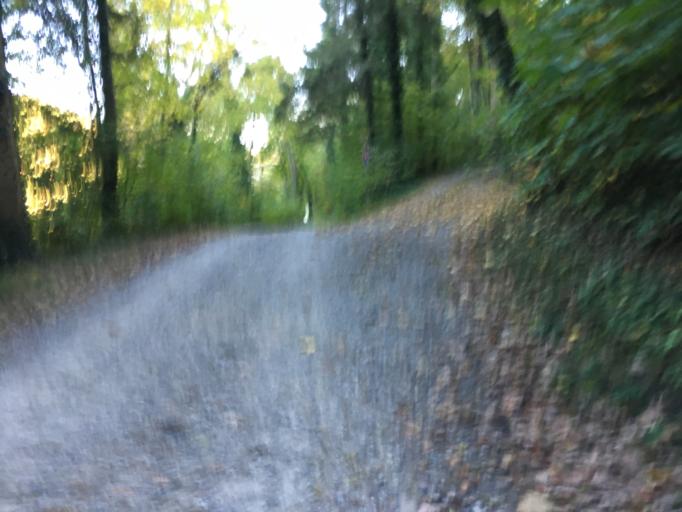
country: CH
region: Zurich
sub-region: Bezirk Buelach
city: Buelach / Soligaenter
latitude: 47.5561
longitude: 8.5496
